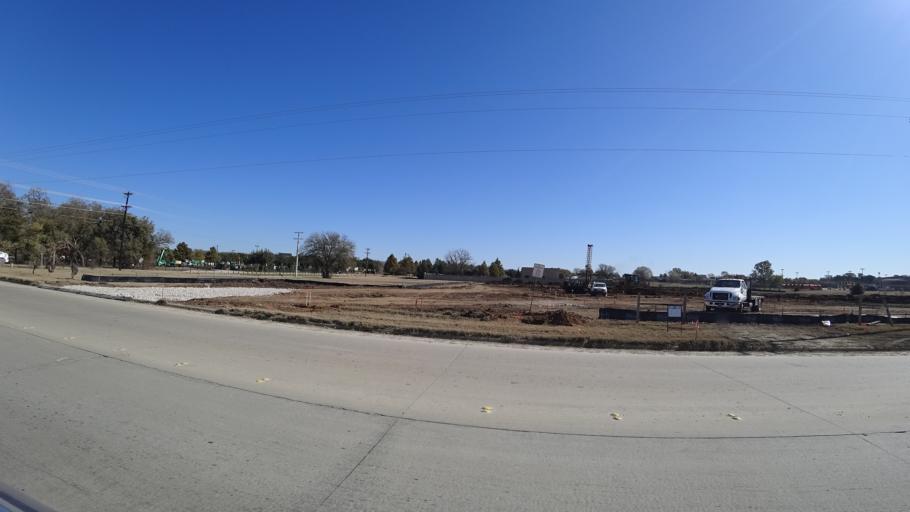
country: US
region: Texas
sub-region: Denton County
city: Lewisville
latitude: 33.0461
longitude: -96.9453
